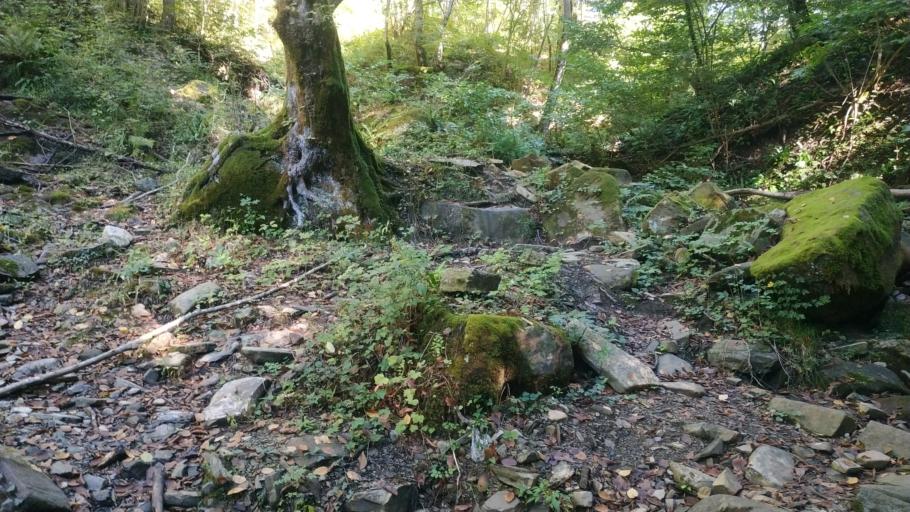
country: RU
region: Krasnodarskiy
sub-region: Sochi City
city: Lazarevskoye
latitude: 43.9790
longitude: 39.4190
